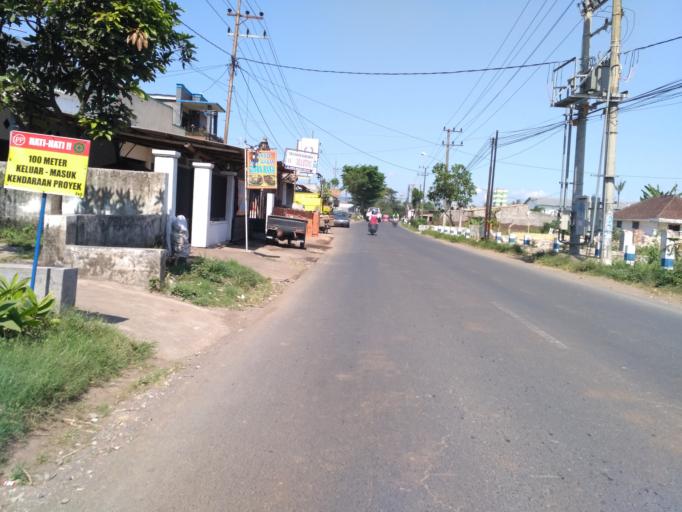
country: ID
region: East Java
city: Tamiajeng
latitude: -7.9549
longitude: 112.7004
